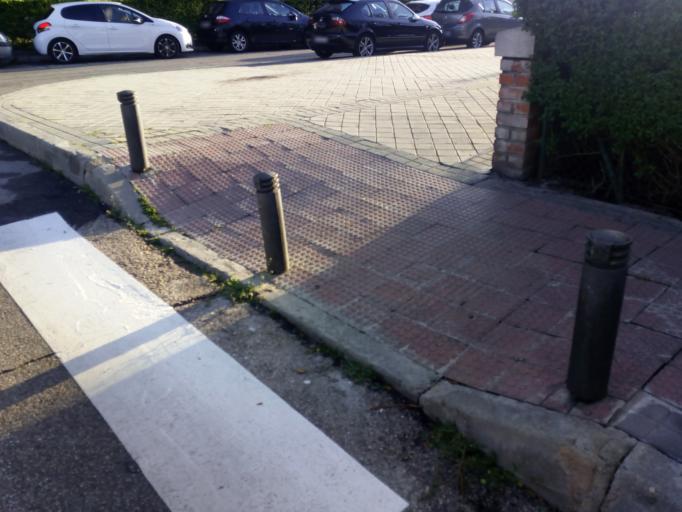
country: ES
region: Madrid
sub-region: Provincia de Madrid
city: Retiro
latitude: 40.4150
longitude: -3.6722
